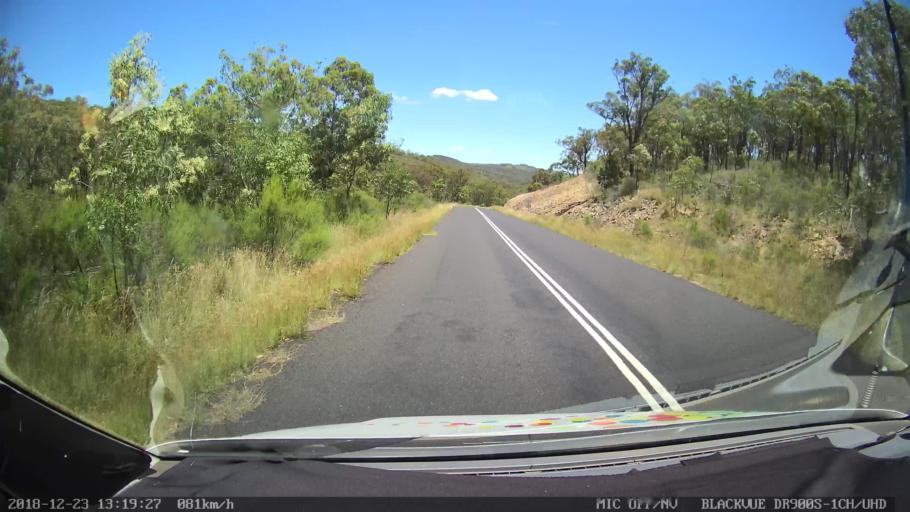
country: AU
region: New South Wales
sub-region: Armidale Dumaresq
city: Armidale
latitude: -30.4826
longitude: 151.4632
